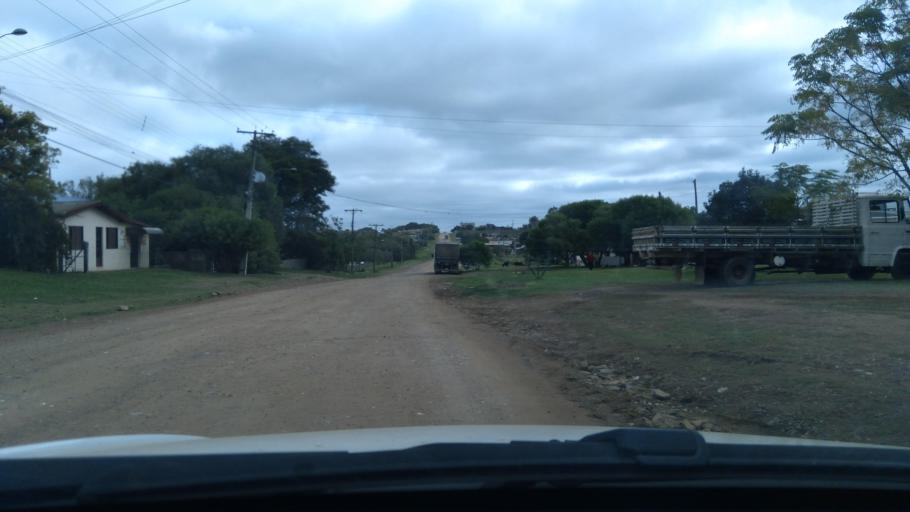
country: BR
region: Rio Grande do Sul
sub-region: Dom Pedrito
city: Dom Pedrito
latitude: -30.9819
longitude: -54.6506
